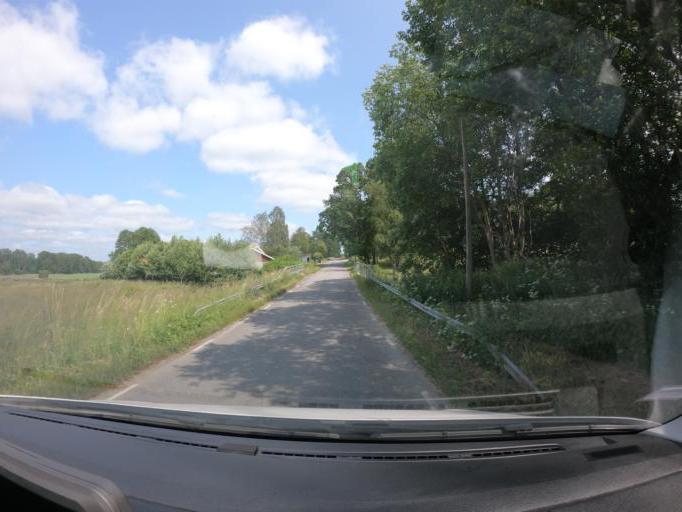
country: SE
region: Skane
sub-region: Hassleholms Kommun
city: Sosdala
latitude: 56.0314
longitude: 13.6378
